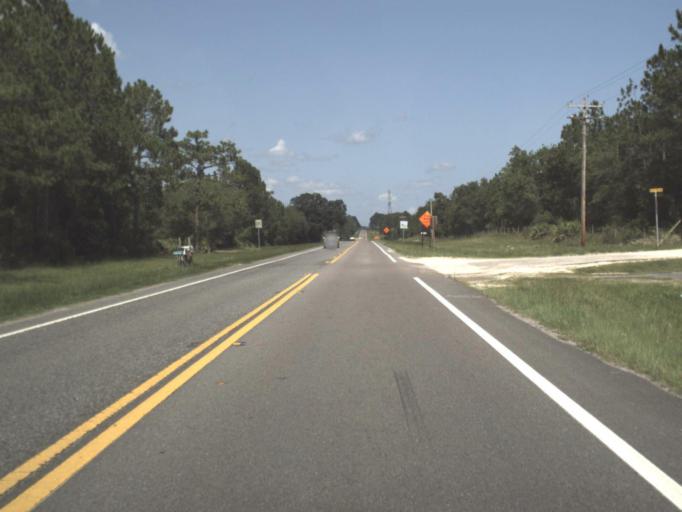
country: US
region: Florida
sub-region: Clay County
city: Asbury Lake
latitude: 29.9830
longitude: -81.7652
